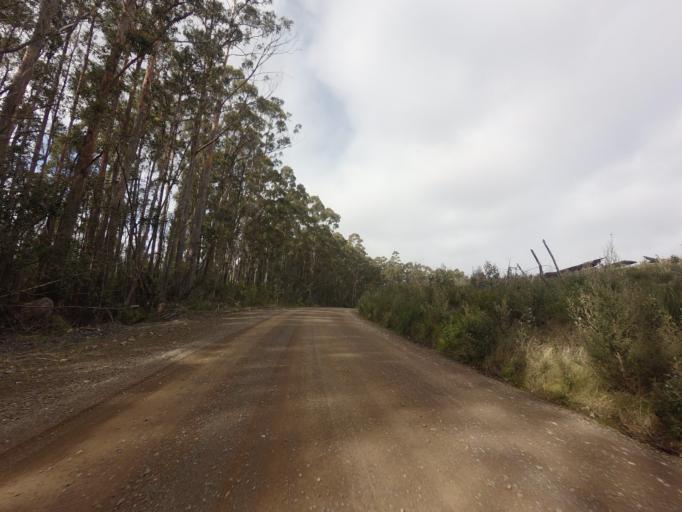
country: AU
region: Tasmania
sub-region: Huon Valley
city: Geeveston
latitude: -43.4867
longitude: 146.8915
